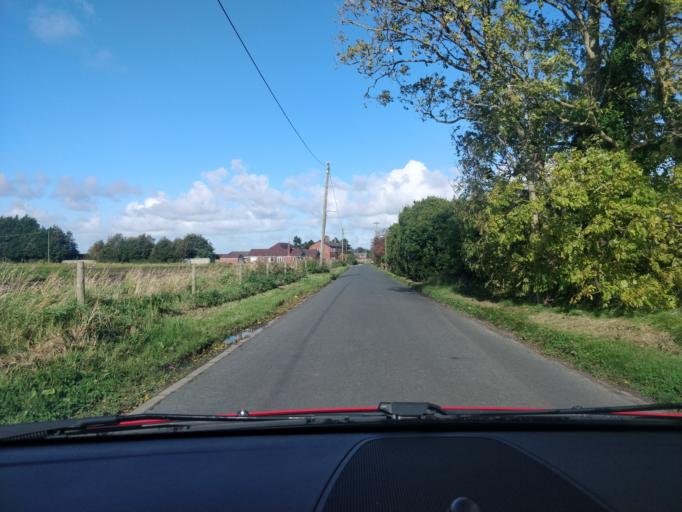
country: GB
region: England
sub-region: Lancashire
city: Banks
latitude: 53.6206
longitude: -2.9388
